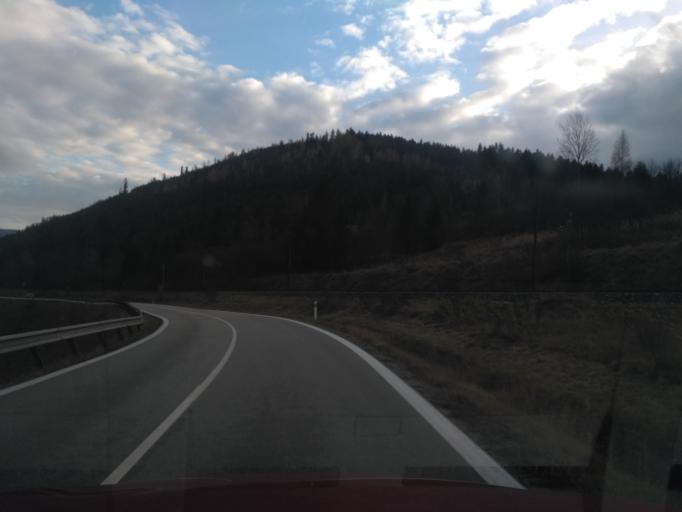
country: SK
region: Kosicky
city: Spisska Nova Ves
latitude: 48.8340
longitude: 20.6462
